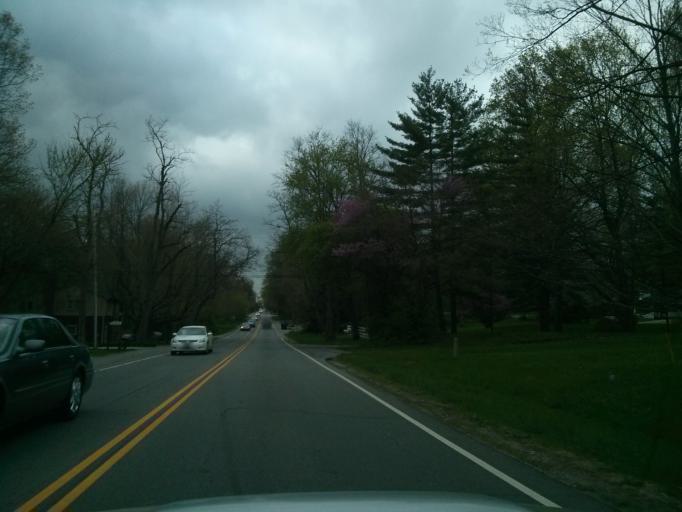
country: US
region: Indiana
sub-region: Hamilton County
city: Carmel
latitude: 39.9517
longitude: -86.1269
